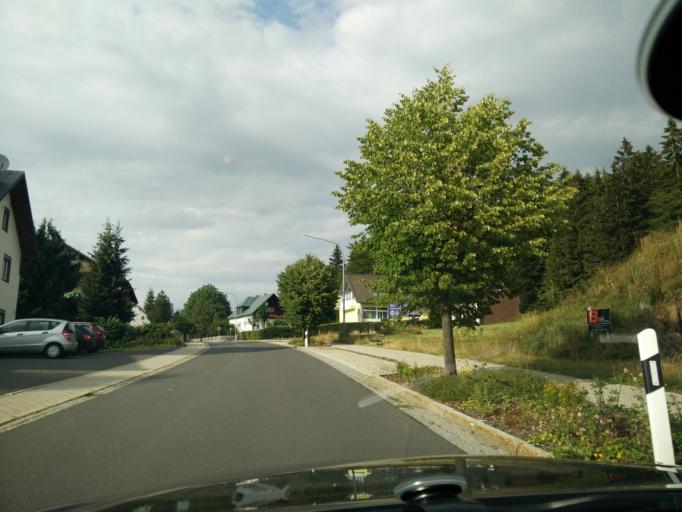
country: DE
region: Bavaria
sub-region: Upper Franconia
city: Fichtelberg
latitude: 50.0146
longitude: 11.8528
